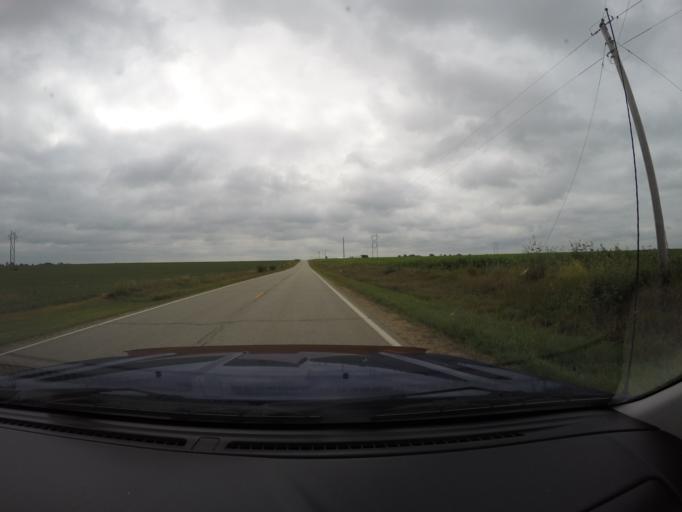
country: US
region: Kansas
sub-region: Morris County
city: Council Grove
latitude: 38.8408
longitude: -96.5293
